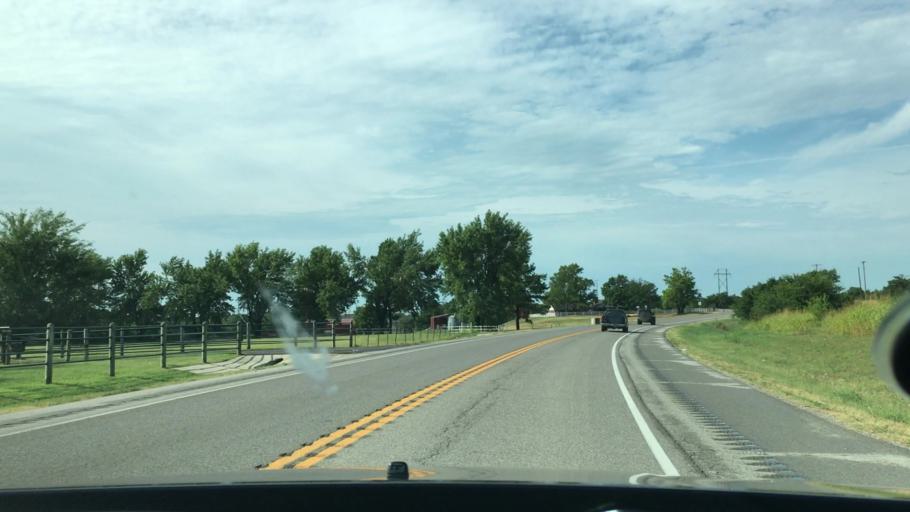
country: US
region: Oklahoma
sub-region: Murray County
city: Sulphur
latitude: 34.5311
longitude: -96.9676
